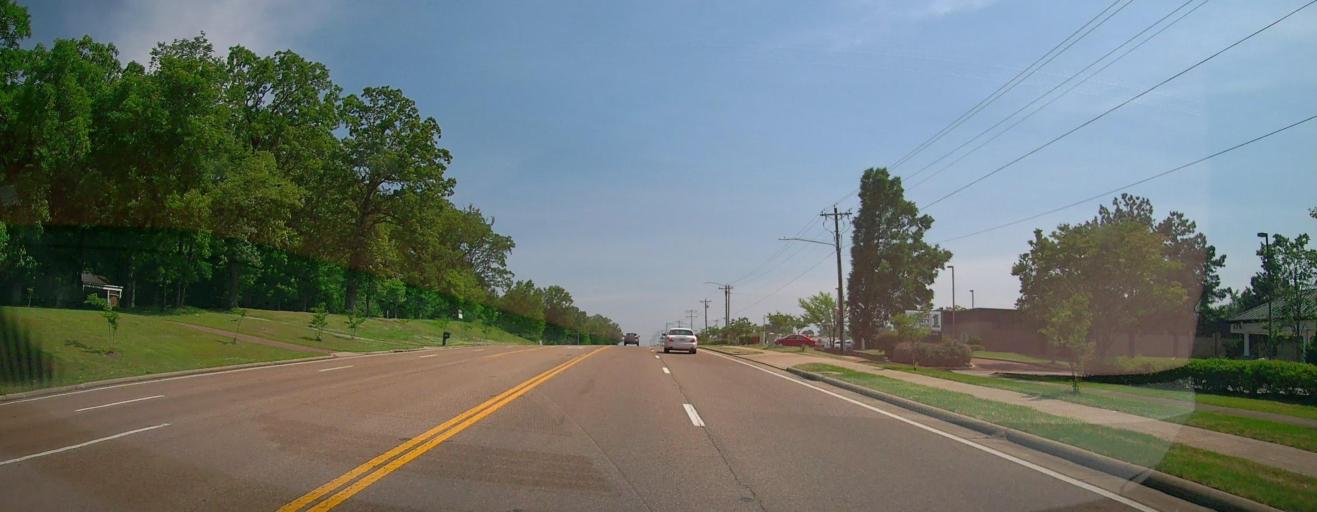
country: US
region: Mississippi
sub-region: De Soto County
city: Olive Branch
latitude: 34.9577
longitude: -89.8304
